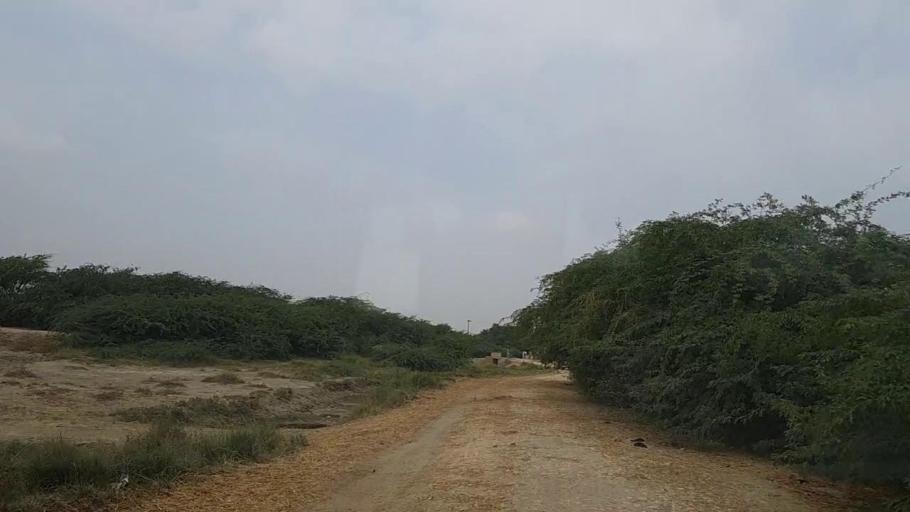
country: PK
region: Sindh
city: Mirpur Sakro
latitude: 24.6023
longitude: 67.6985
